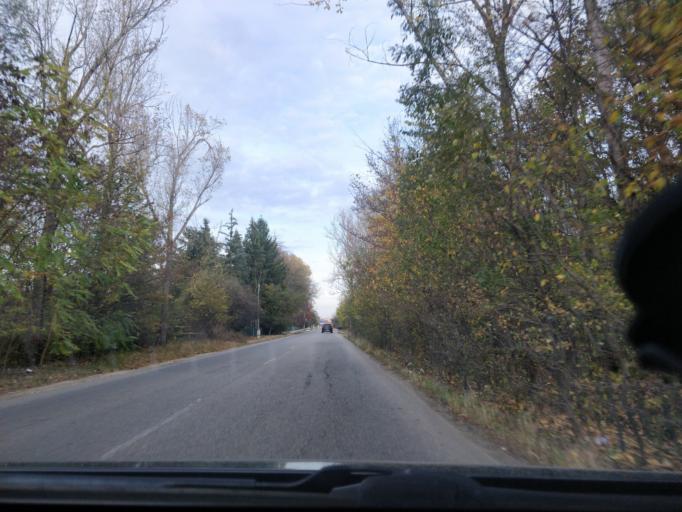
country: RO
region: Giurgiu
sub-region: Comuna Bolintin Vale
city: Malu Spart
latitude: 44.4364
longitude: 25.6905
